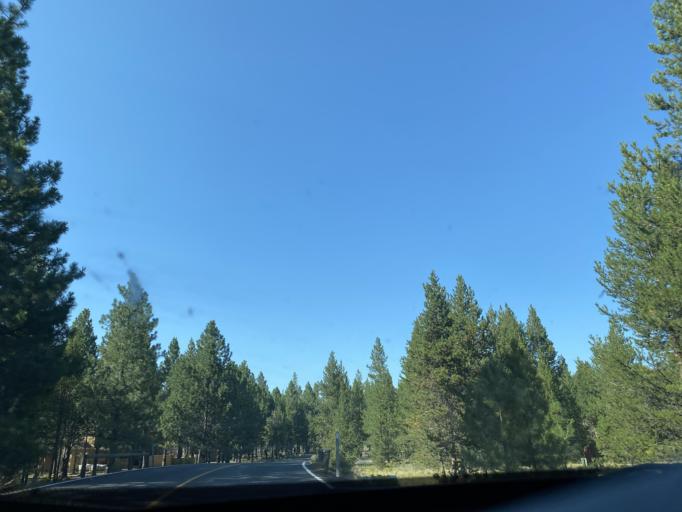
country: US
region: Oregon
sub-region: Deschutes County
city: Sunriver
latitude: 43.8835
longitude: -121.4401
